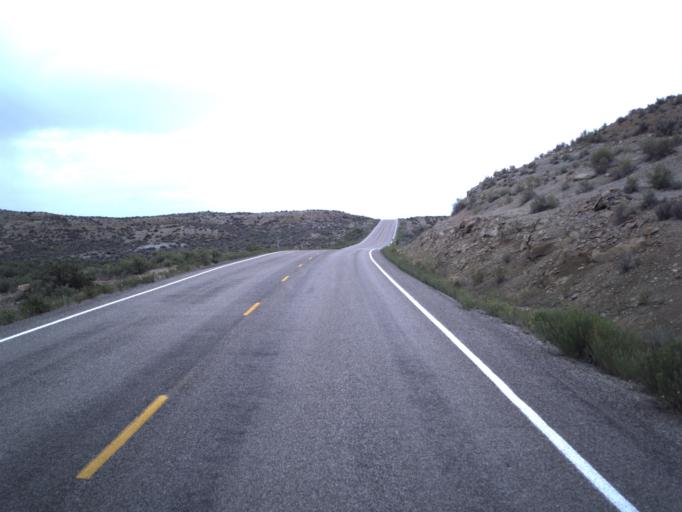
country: US
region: Colorado
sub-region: Rio Blanco County
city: Rangely
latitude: 40.0615
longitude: -109.1970
